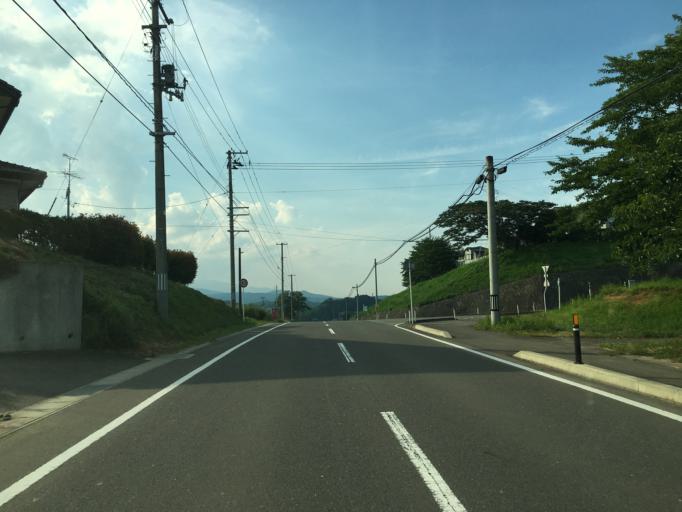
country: JP
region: Fukushima
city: Nihommatsu
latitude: 37.5566
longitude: 140.4312
